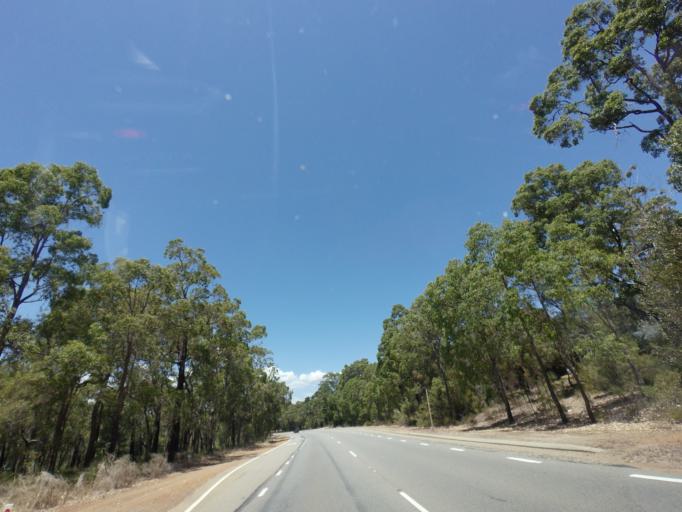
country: AU
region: Western Australia
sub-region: Mundaring
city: Parkerville
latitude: -31.9001
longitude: 116.1292
